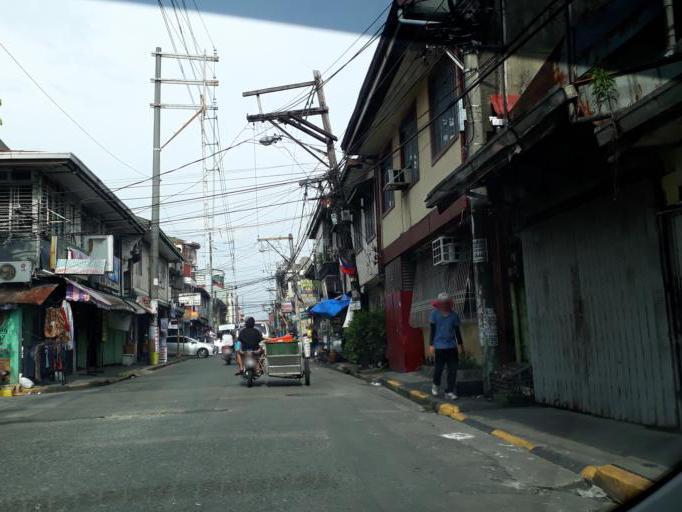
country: PH
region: Metro Manila
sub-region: City of Manila
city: Manila
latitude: 14.6363
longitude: 120.9797
